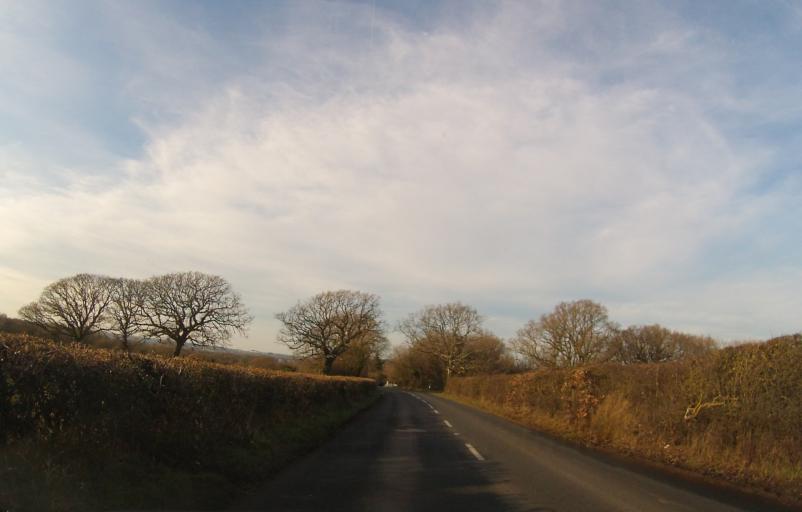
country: GB
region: England
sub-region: Isle of Wight
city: Newport
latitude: 50.7196
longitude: -1.2499
